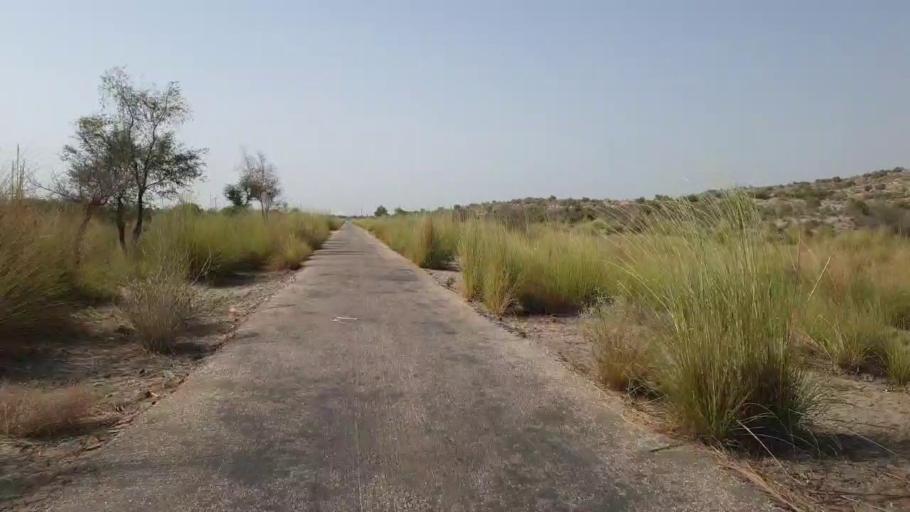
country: PK
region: Sindh
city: Jam Sahib
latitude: 26.5744
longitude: 68.9216
